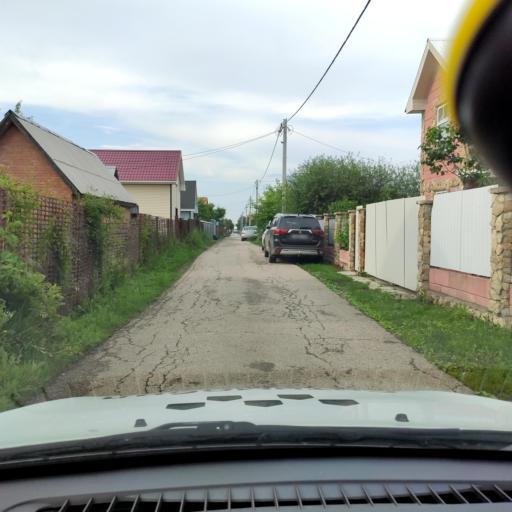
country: RU
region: Samara
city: Podstepki
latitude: 53.5776
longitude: 49.0793
